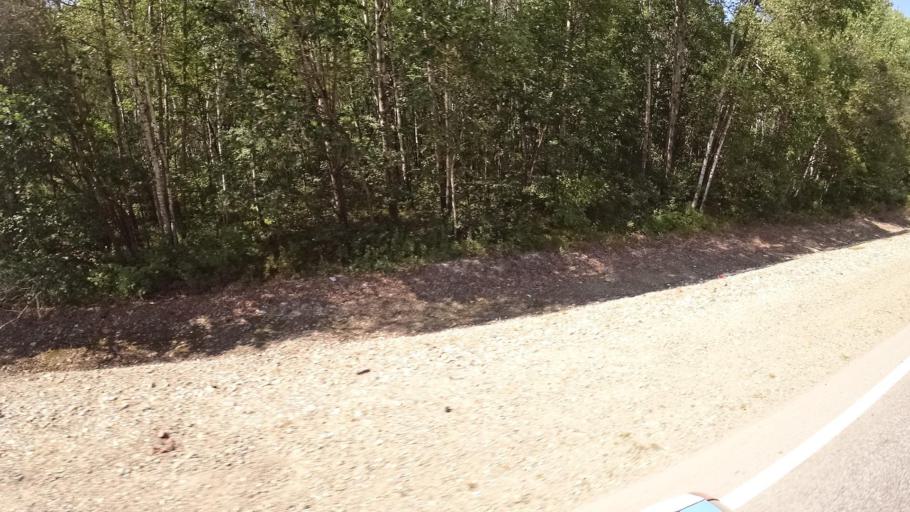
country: RU
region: Khabarovsk Krai
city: Khor
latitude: 47.9819
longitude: 135.0871
